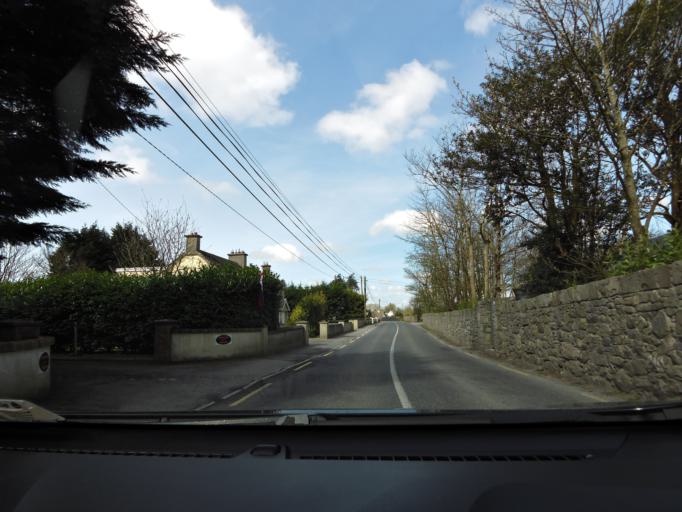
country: IE
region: Connaught
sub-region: County Galway
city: Athenry
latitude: 53.3004
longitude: -8.7631
